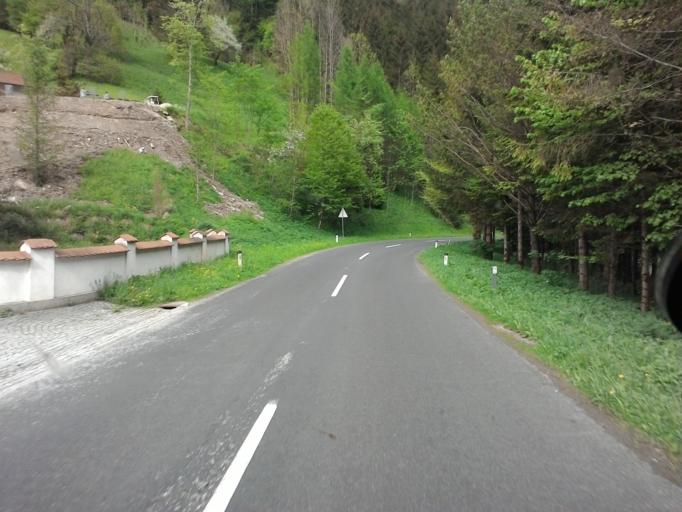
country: AT
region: Styria
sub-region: Politischer Bezirk Liezen
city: Sankt Gallen
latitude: 47.7171
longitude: 14.5680
